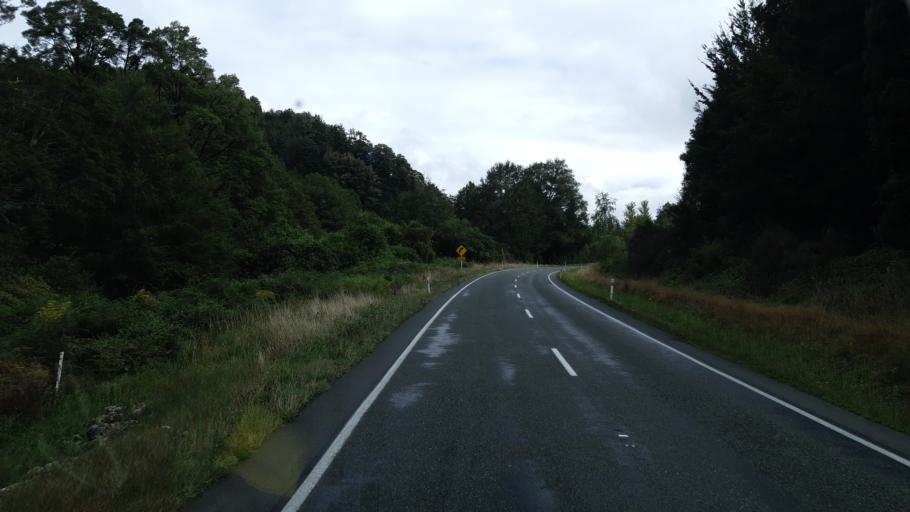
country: NZ
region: West Coast
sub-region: Buller District
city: Westport
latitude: -41.8213
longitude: 172.2340
